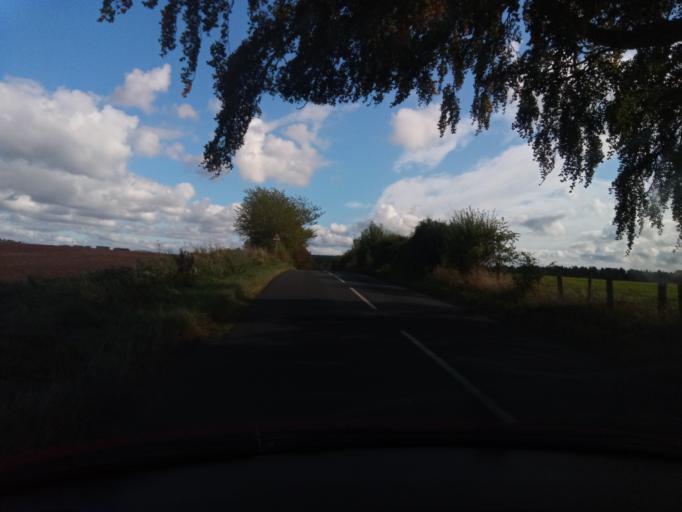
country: GB
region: Scotland
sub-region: The Scottish Borders
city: Kelso
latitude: 55.5740
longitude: -2.3959
